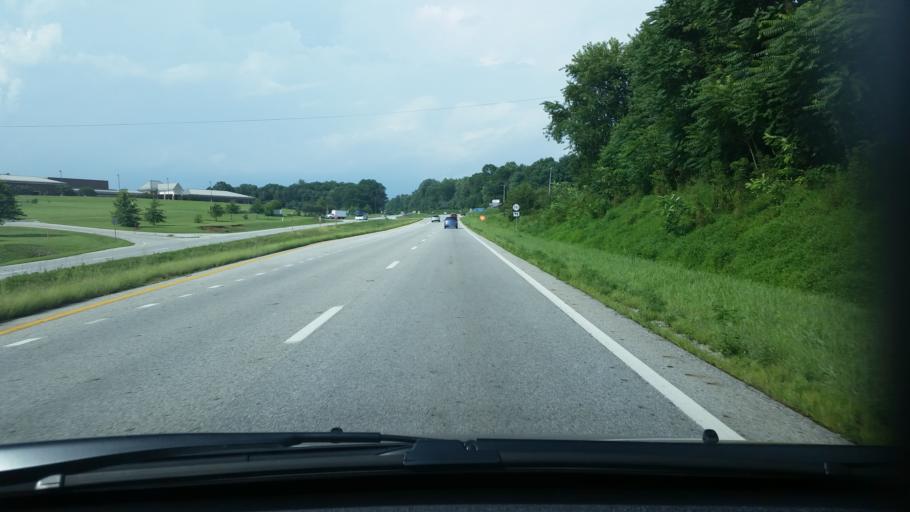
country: US
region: Virginia
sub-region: Nelson County
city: Lovingston
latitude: 37.7296
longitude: -78.8958
